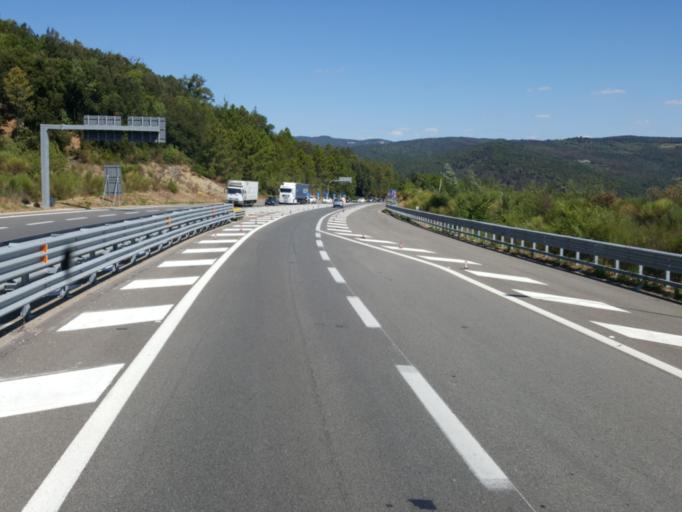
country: IT
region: Tuscany
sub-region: Provincia di Grosseto
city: Civitella Marittima
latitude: 42.9983
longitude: 11.2874
